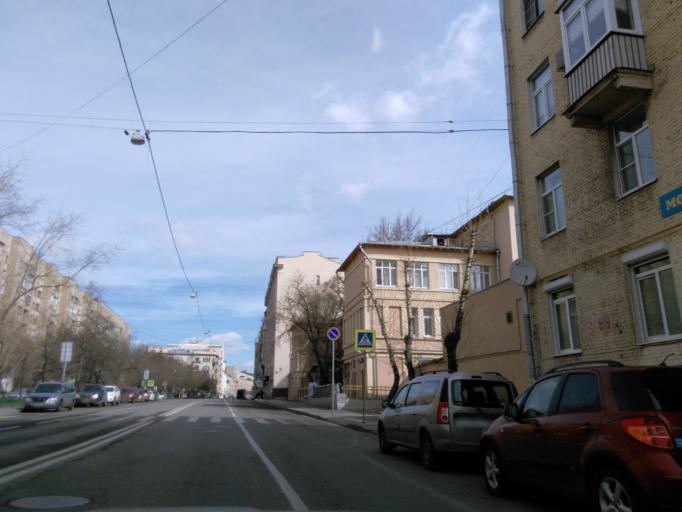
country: RU
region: Moskovskaya
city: Dorogomilovo
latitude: 55.7399
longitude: 37.5766
